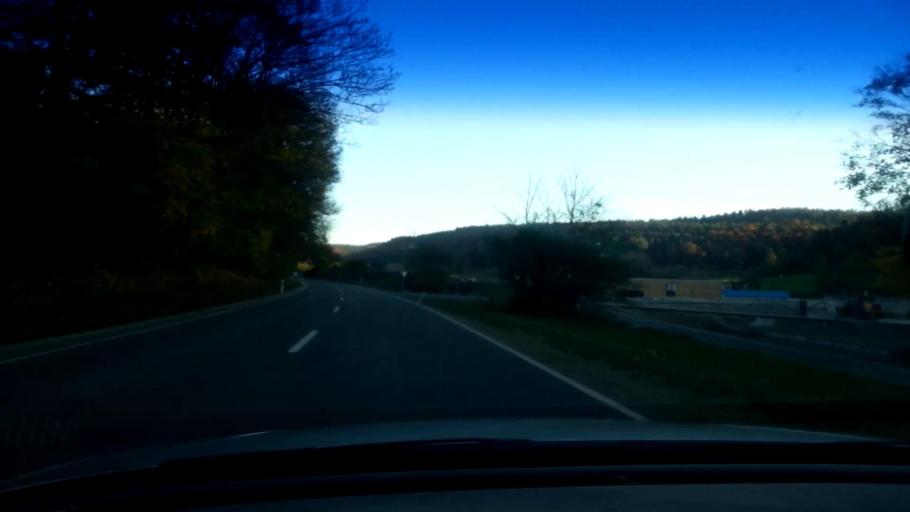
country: DE
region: Bavaria
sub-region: Upper Franconia
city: Heiligenstadt
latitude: 49.8528
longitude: 11.1820
